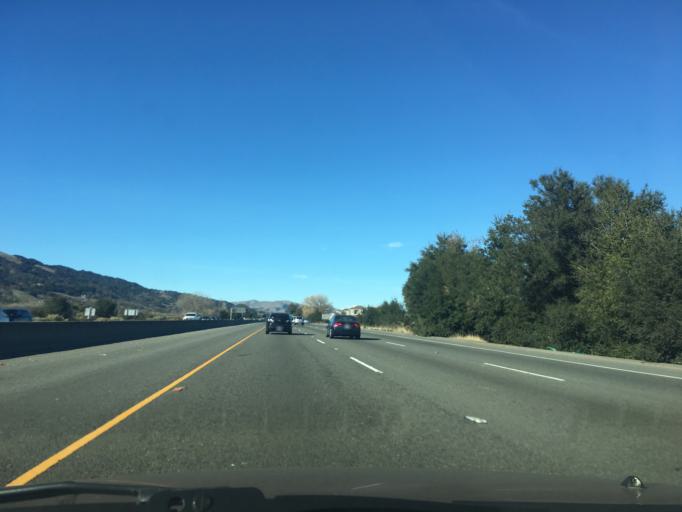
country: US
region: California
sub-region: Alameda County
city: Pleasanton
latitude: 37.6497
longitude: -121.8941
